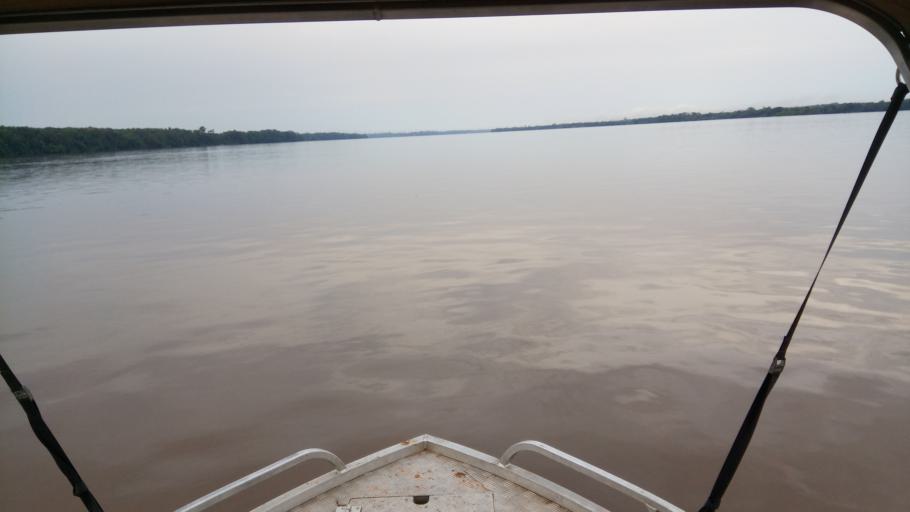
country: CD
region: Eastern Province
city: Kisangani
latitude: 0.5740
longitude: 24.8331
